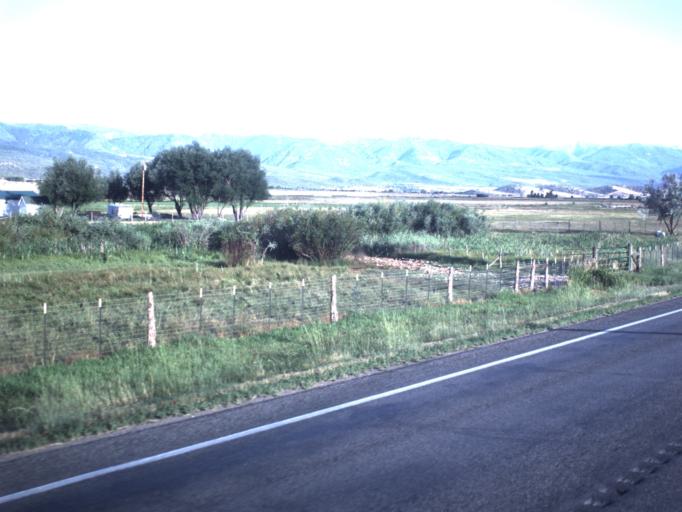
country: US
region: Utah
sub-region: Sanpete County
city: Fairview
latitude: 39.6119
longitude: -111.4447
